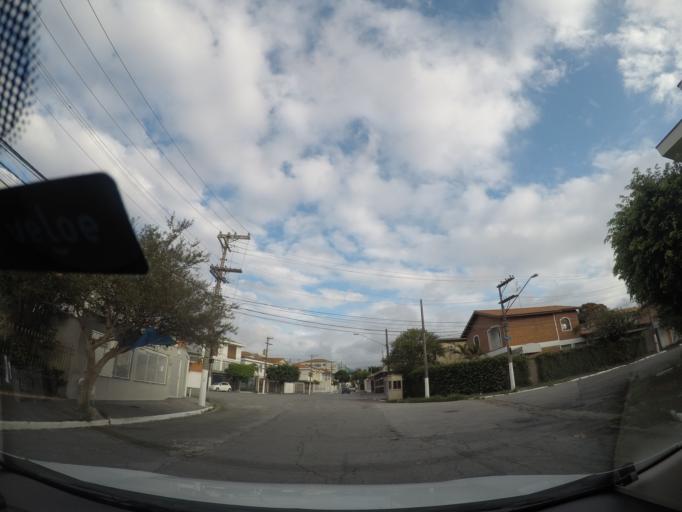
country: BR
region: Sao Paulo
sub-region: Diadema
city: Diadema
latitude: -23.6245
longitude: -46.6522
